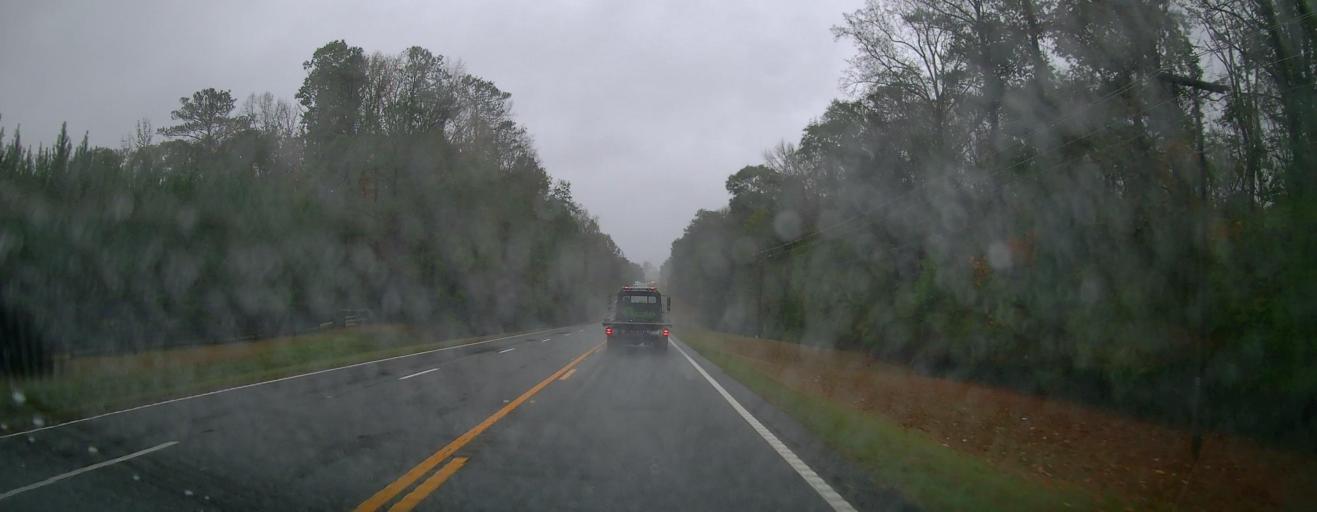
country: US
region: Georgia
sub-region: Jones County
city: Gray
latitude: 33.0459
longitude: -83.5094
